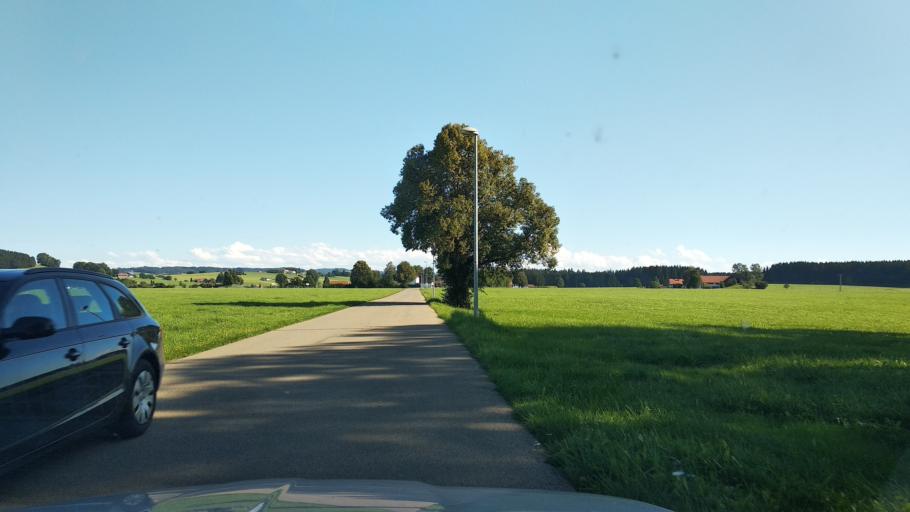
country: DE
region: Baden-Wuerttemberg
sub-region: Tuebingen Region
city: Leutkirch im Allgau
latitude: 47.8154
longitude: 10.0601
